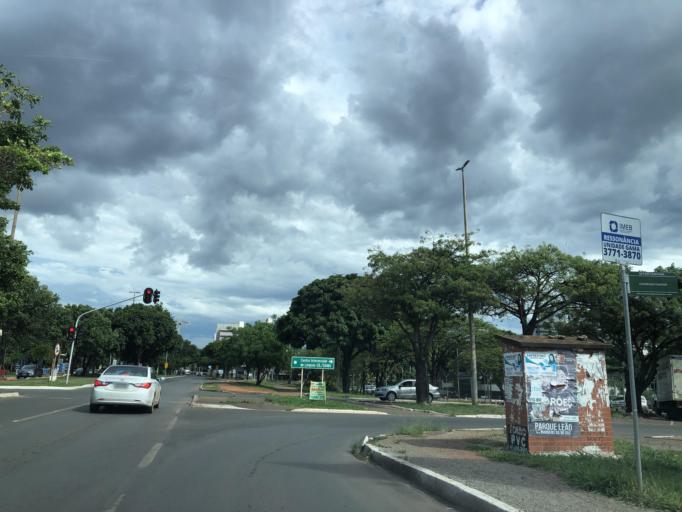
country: BR
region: Goias
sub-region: Luziania
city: Luziania
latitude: -16.0162
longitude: -48.0661
